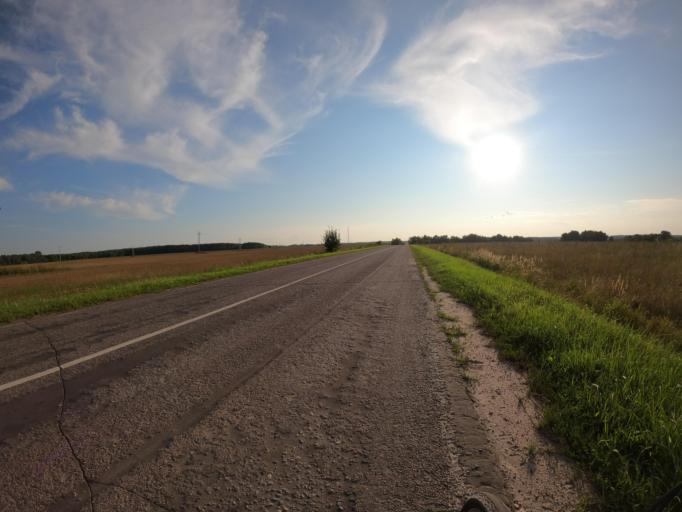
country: RU
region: Moskovskaya
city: Meshcherino
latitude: 55.1284
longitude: 38.3586
